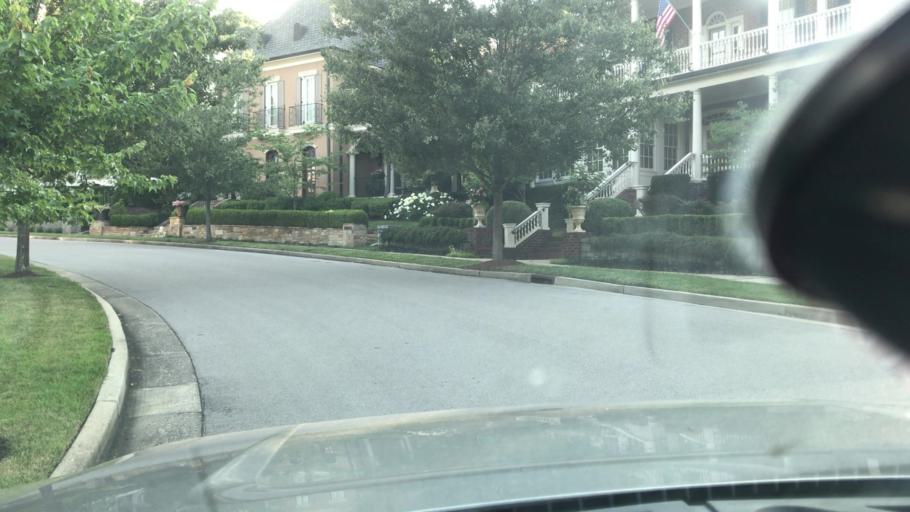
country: US
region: Tennessee
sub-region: Williamson County
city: Brentwood
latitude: 36.0080
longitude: -86.8332
